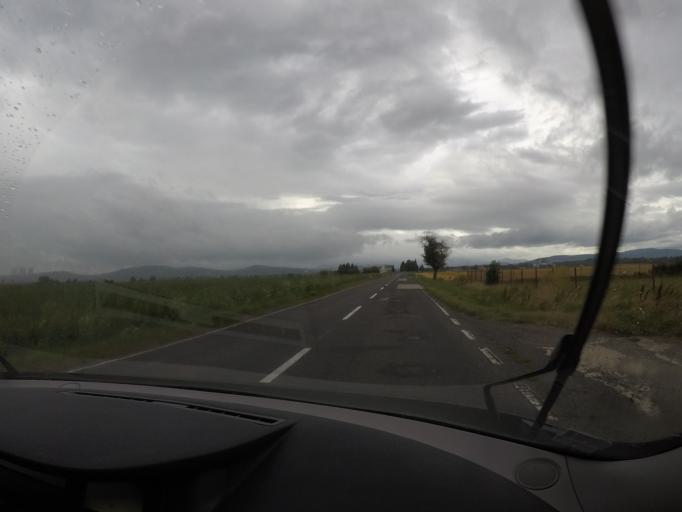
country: SK
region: Nitriansky
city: Tlmace
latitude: 48.2223
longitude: 18.5195
